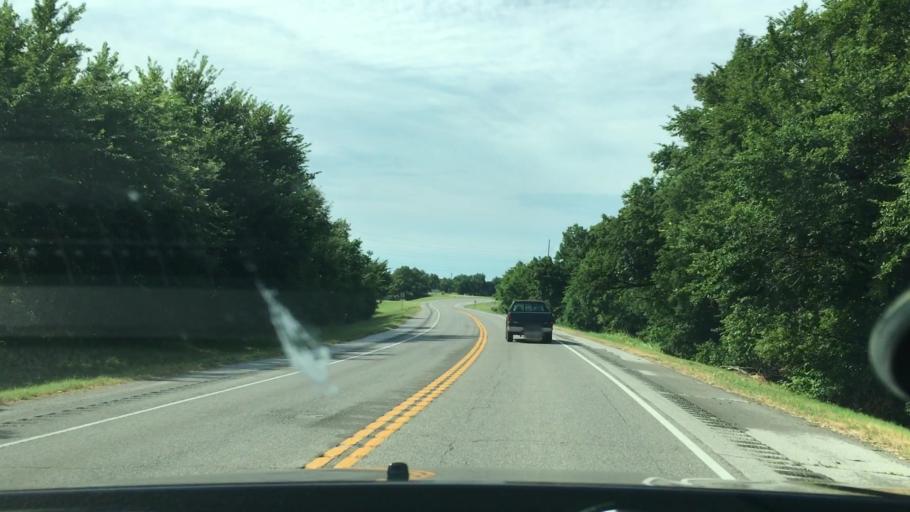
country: US
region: Oklahoma
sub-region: Murray County
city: Sulphur
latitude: 34.5251
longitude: -96.9700
